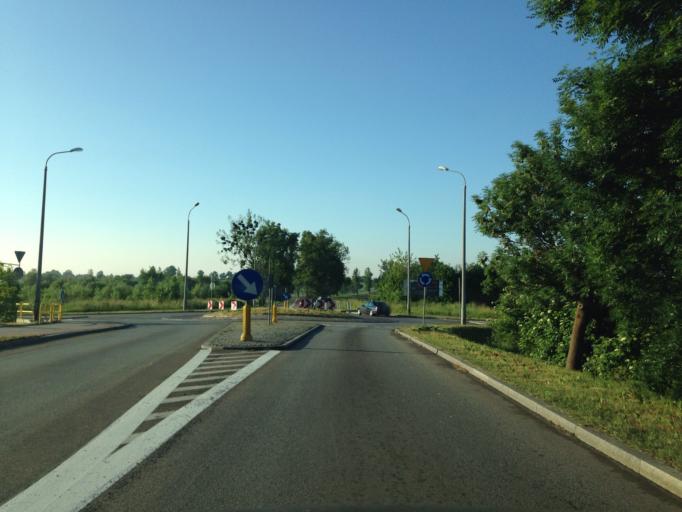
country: PL
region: Pomeranian Voivodeship
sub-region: Powiat kwidzynski
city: Kwidzyn
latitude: 53.6988
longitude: 18.9641
